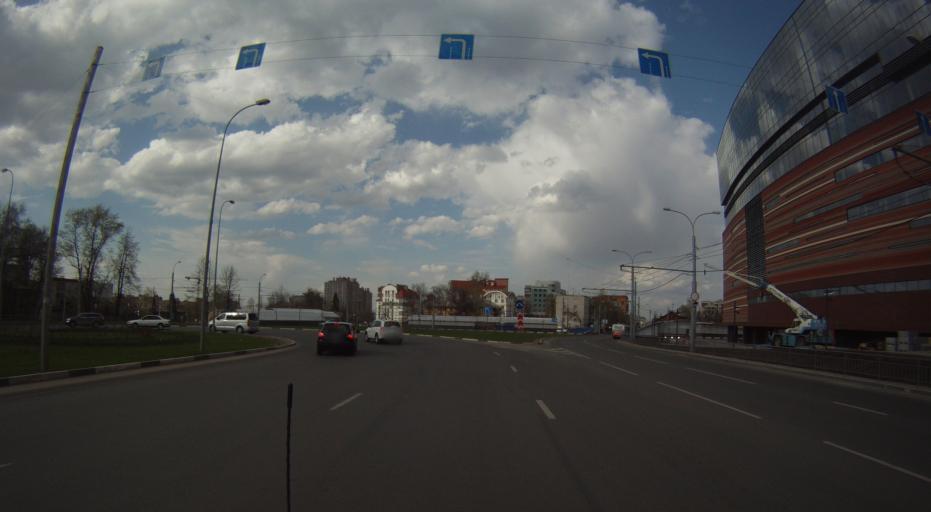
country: RU
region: Nizjnij Novgorod
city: Nizhniy Novgorod
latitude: 56.3090
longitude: 43.9856
